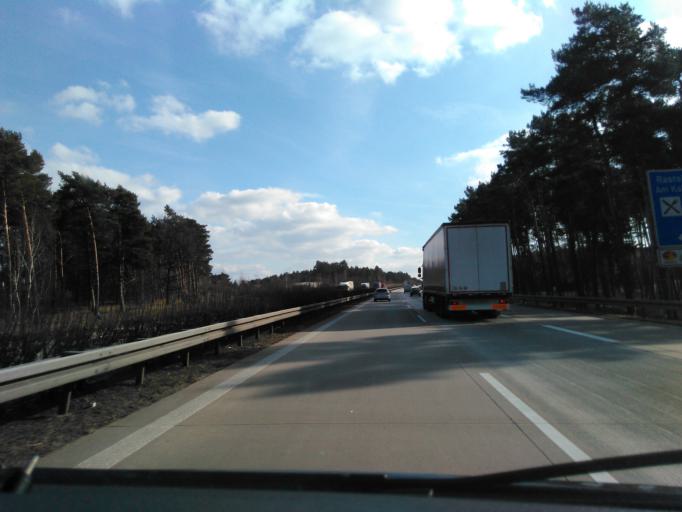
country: DE
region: Brandenburg
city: Bestensee
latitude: 52.2120
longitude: 13.6052
